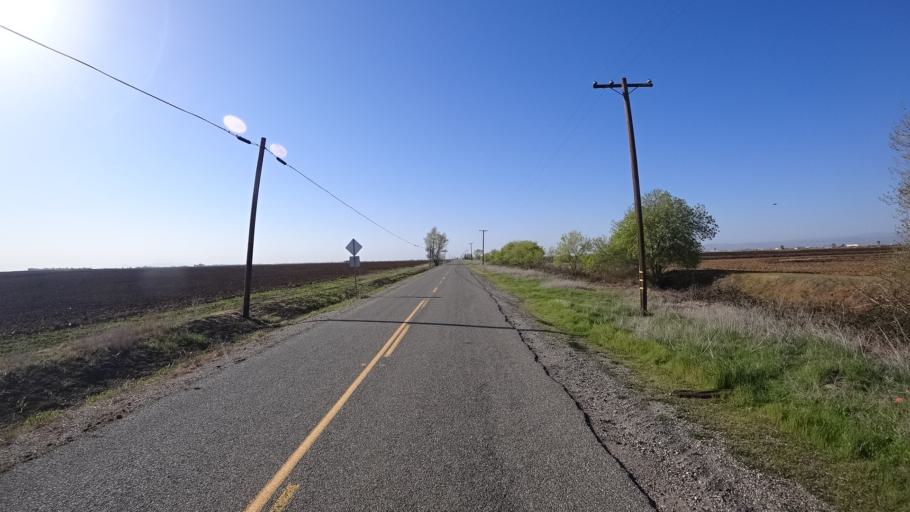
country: US
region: California
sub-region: Glenn County
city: Willows
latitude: 39.5082
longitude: -122.1745
